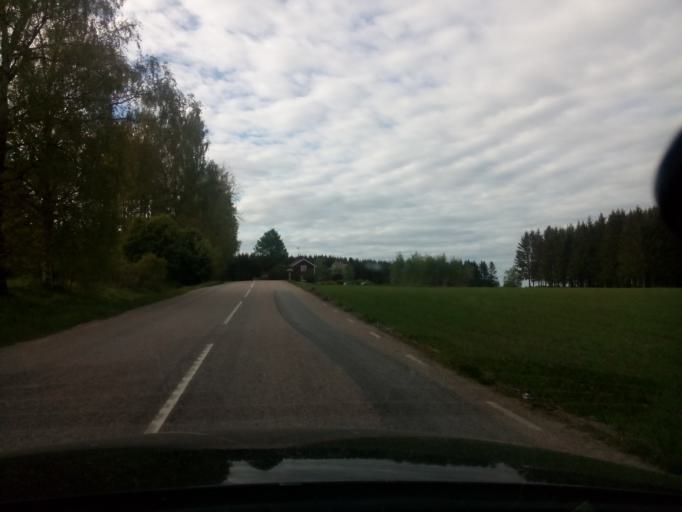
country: SE
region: Soedermanland
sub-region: Nykopings Kommun
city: Nykoping
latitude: 58.8397
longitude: 16.9356
